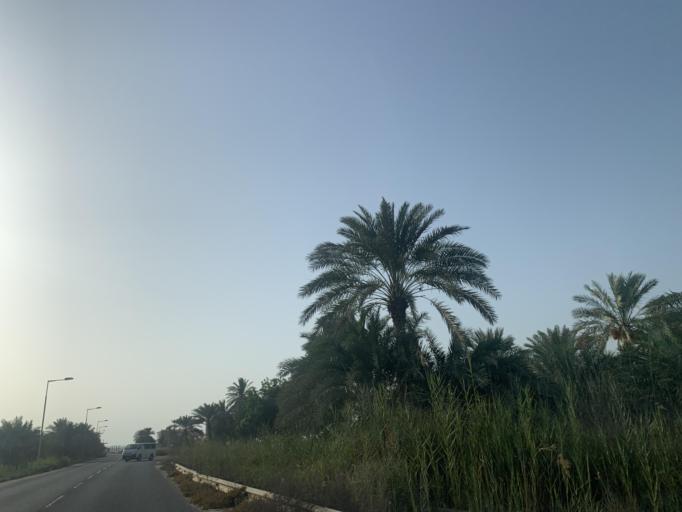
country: BH
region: Central Governorate
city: Madinat Hamad
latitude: 26.1783
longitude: 50.4559
